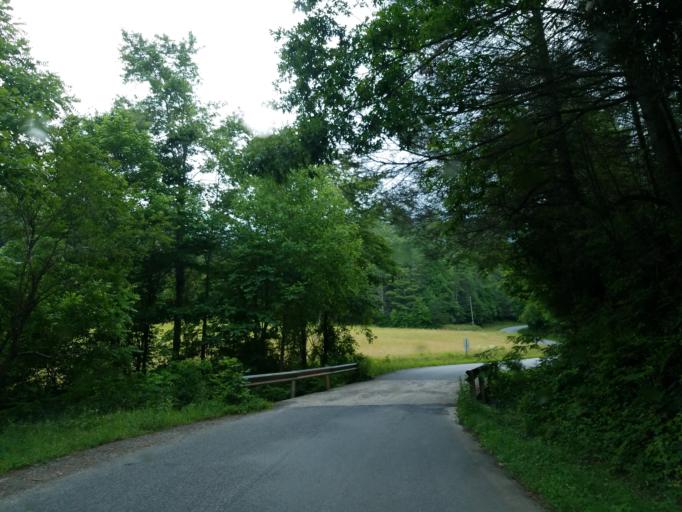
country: US
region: Georgia
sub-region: Fannin County
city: Blue Ridge
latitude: 34.7809
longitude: -84.3696
